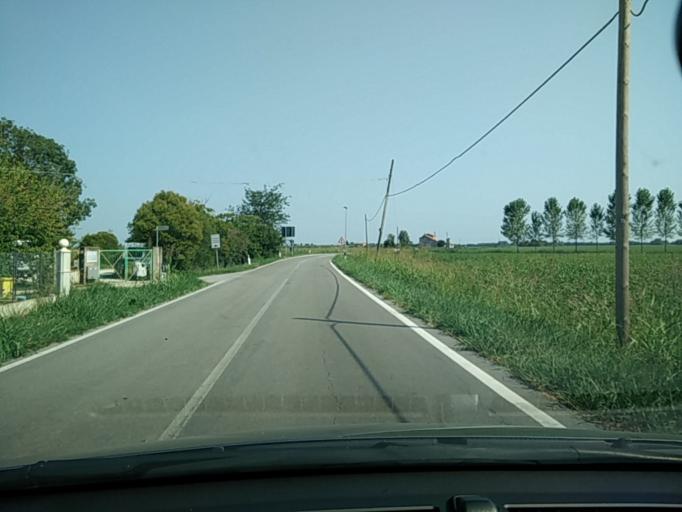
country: IT
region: Veneto
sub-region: Provincia di Venezia
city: La Salute di Livenza
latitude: 45.6440
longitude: 12.8239
